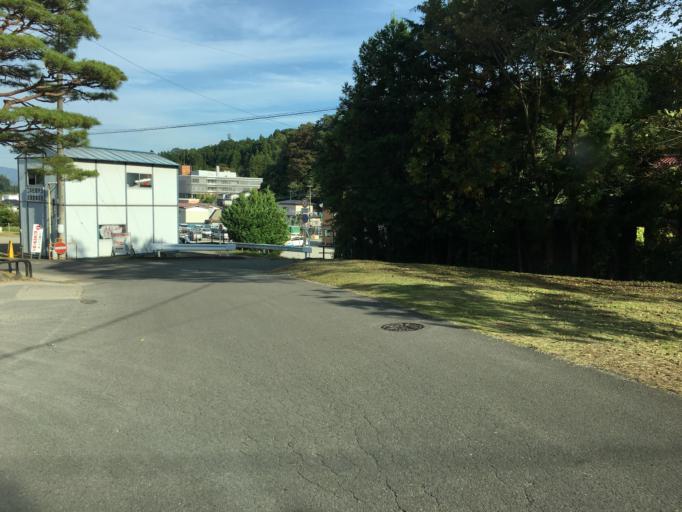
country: JP
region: Fukushima
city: Nihommatsu
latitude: 37.5965
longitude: 140.4305
